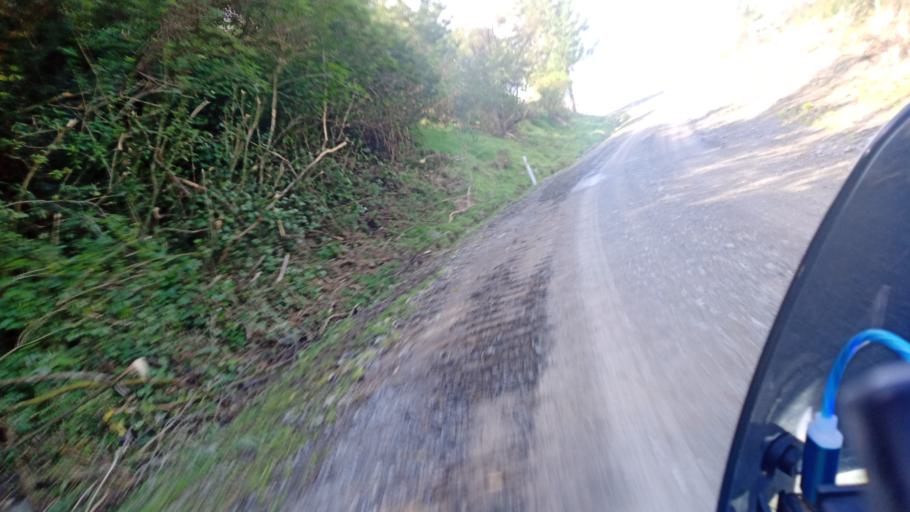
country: NZ
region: Gisborne
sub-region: Gisborne District
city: Gisborne
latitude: -37.8522
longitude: 178.0834
